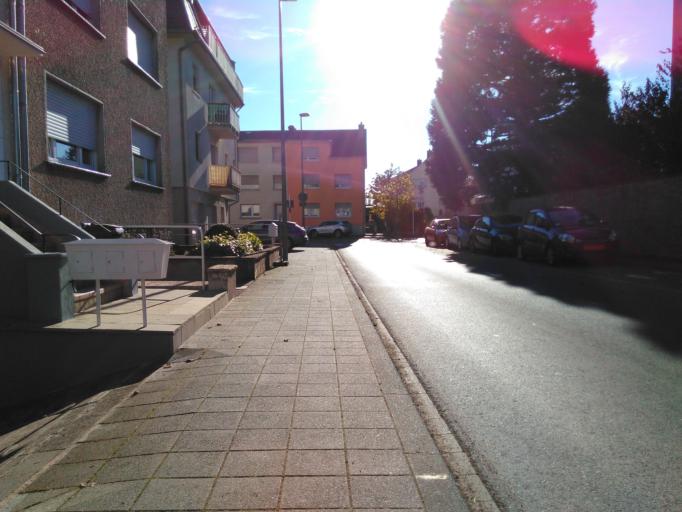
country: LU
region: Luxembourg
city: Belvaux
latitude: 49.5078
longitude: 5.9274
